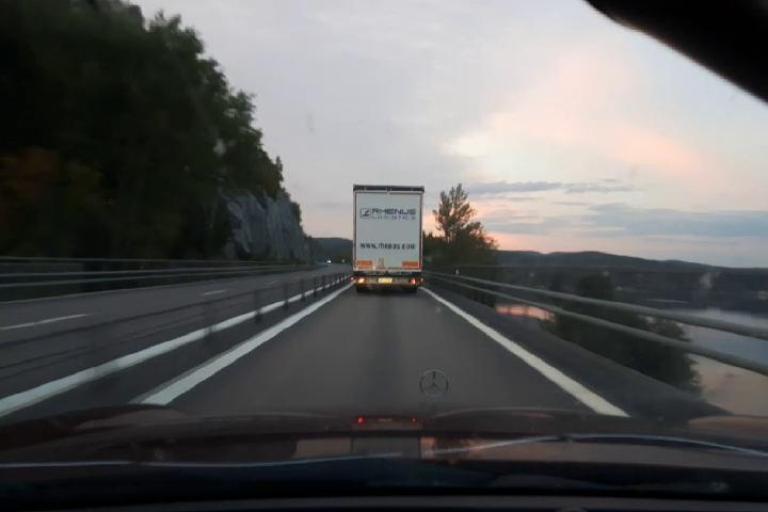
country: SE
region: Vaesternorrland
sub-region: Haernoesands Kommun
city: Haernoesand
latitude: 62.8256
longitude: 17.9694
